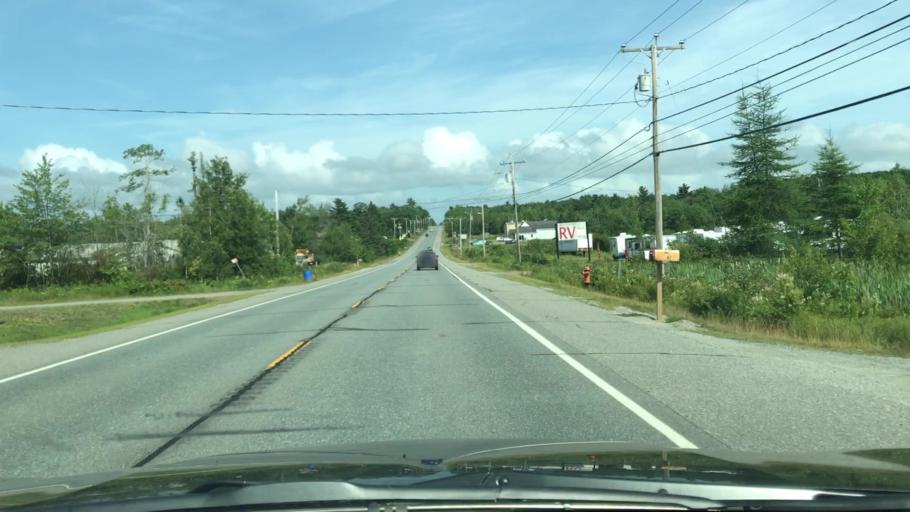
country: US
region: Maine
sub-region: Hancock County
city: Ellsworth
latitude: 44.5395
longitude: -68.4594
